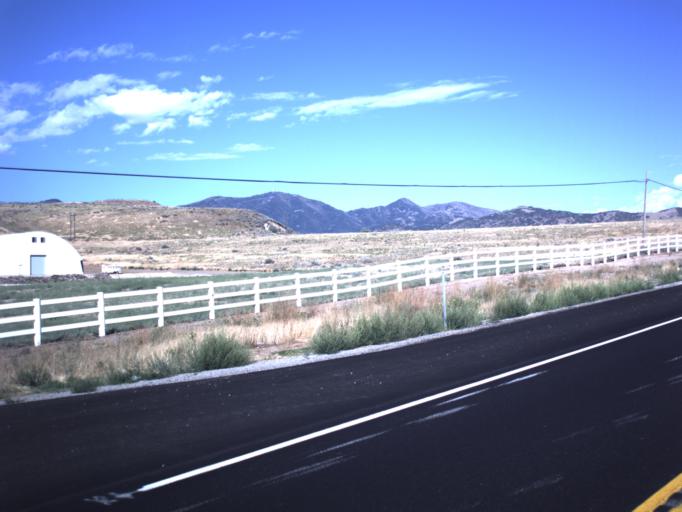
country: US
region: Utah
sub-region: Salt Lake County
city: Oquirrh
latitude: 40.6431
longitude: -112.0641
